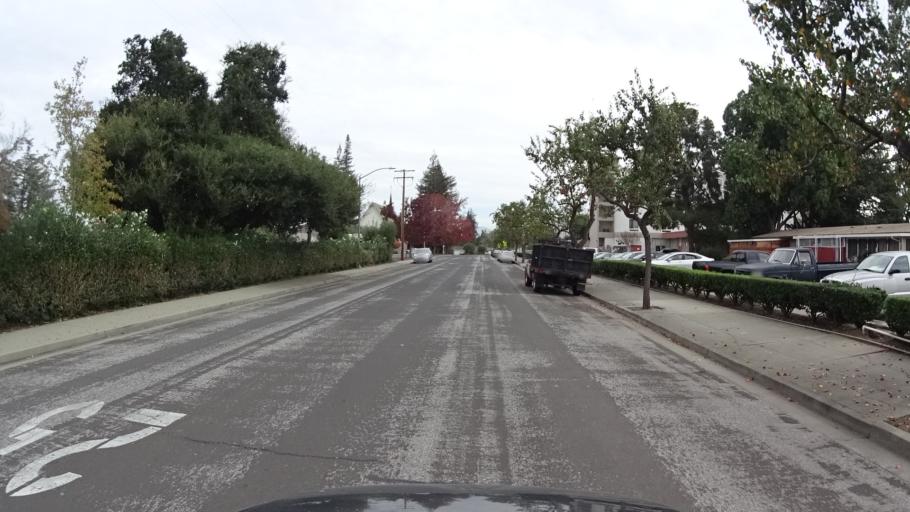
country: US
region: California
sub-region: Santa Clara County
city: Santa Clara
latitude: 37.3329
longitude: -121.9530
